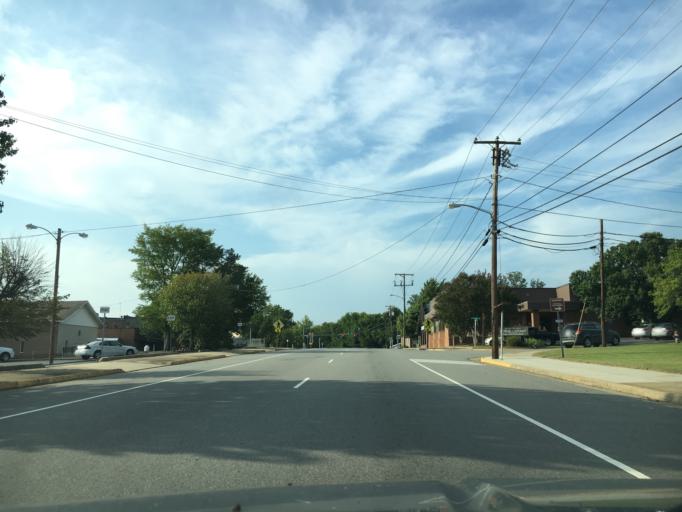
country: US
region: Virginia
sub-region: Halifax County
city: South Boston
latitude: 36.6980
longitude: -78.9000
